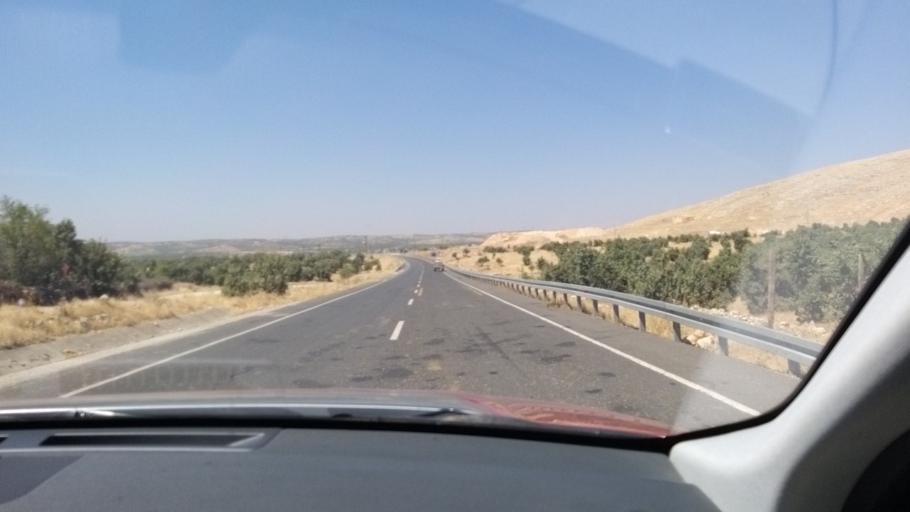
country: TR
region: Mardin
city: Dargecit
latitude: 37.5487
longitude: 41.7468
